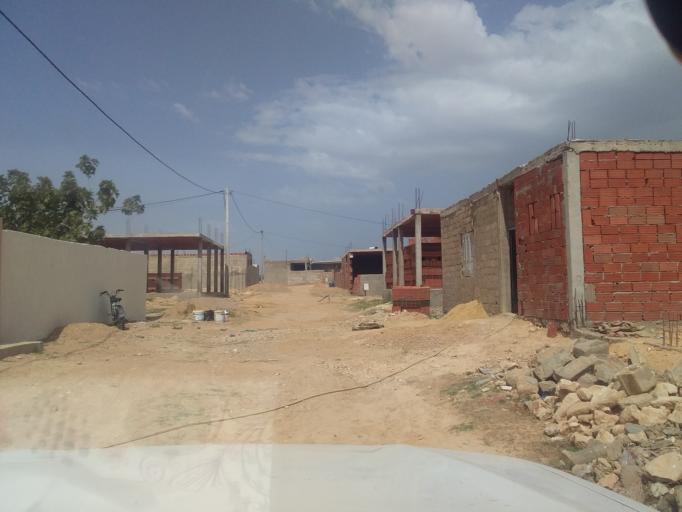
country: TN
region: Madanin
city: Medenine
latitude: 33.5879
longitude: 10.3266
